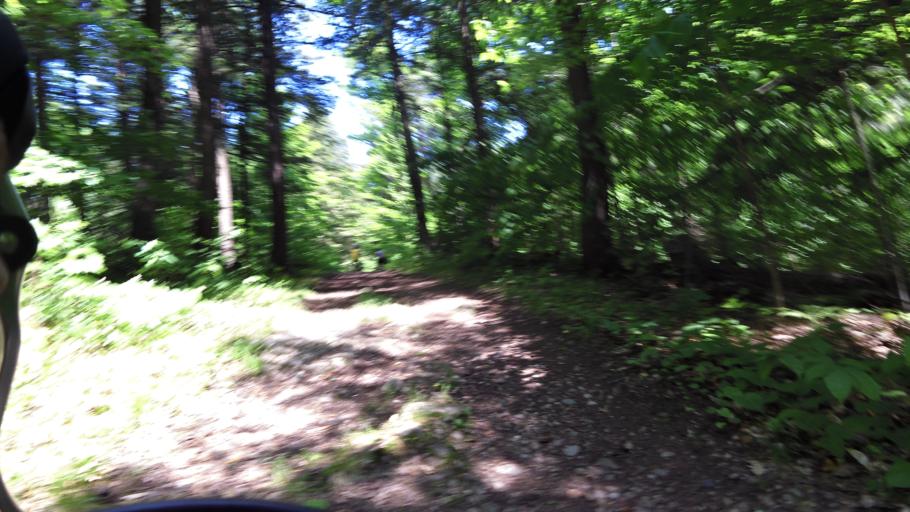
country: CA
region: Quebec
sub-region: Outaouais
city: Wakefield
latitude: 45.5630
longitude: -75.9031
